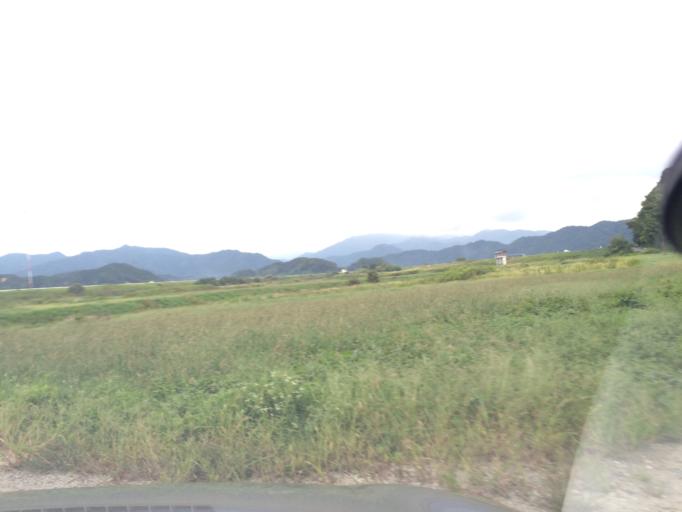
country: JP
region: Hyogo
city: Toyooka
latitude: 35.5041
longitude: 134.8326
